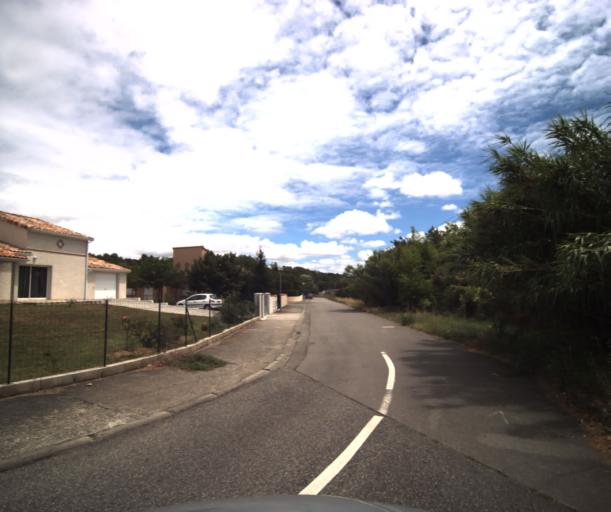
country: FR
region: Midi-Pyrenees
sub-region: Departement de la Haute-Garonne
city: Lacroix-Falgarde
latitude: 43.4852
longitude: 1.4019
